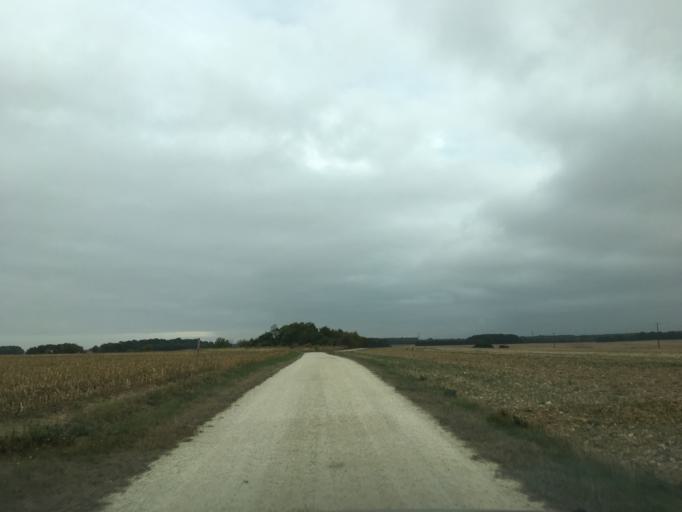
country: FR
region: Poitou-Charentes
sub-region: Departement des Deux-Sevres
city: Beauvoir-sur-Niort
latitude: 46.0833
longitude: -0.4918
